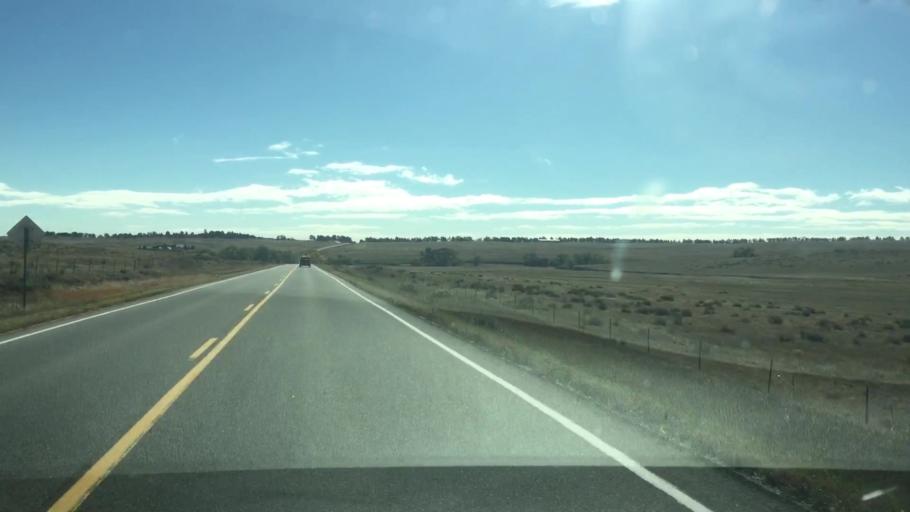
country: US
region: Colorado
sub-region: Elbert County
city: Kiowa
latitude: 39.3243
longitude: -104.3920
